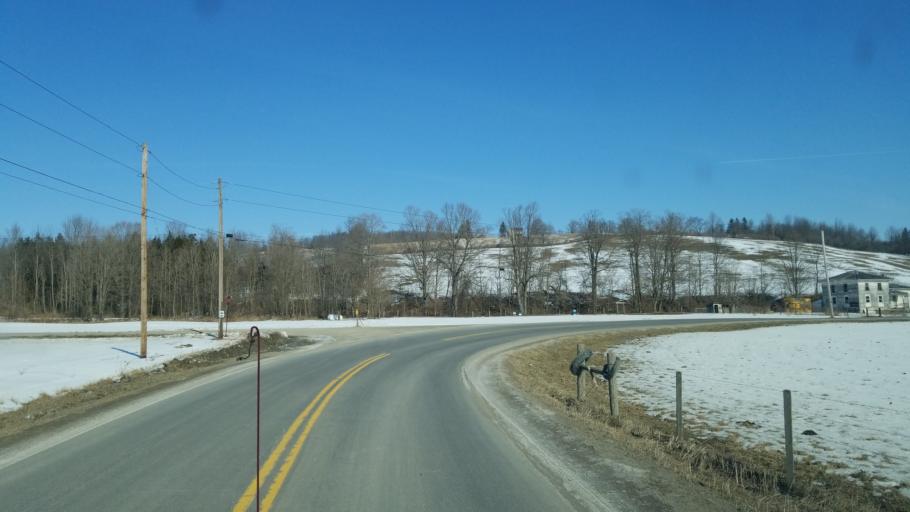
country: US
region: Pennsylvania
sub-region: Tioga County
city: Elkland
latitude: 42.0746
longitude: -77.4301
